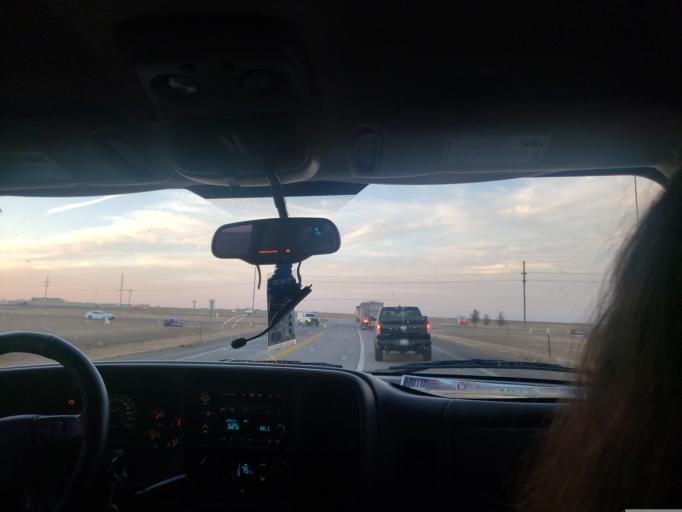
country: US
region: Kansas
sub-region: Seward County
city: Liberal
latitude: 37.0679
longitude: -100.9053
